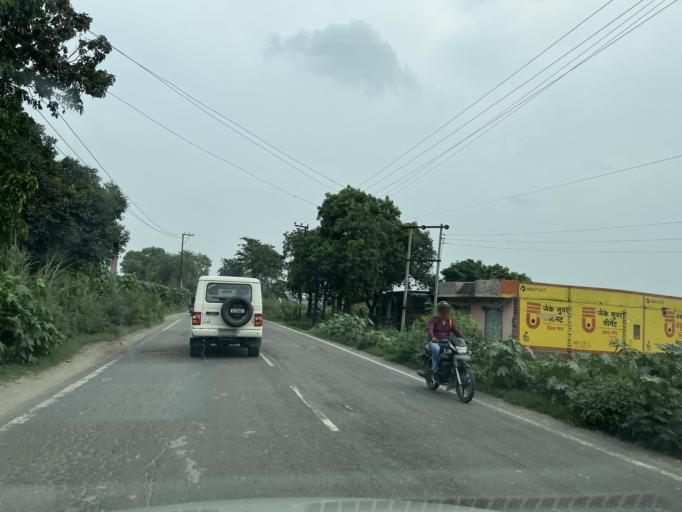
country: IN
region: Uttar Pradesh
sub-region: Rampur
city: Bilaspur
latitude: 29.0256
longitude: 79.2701
